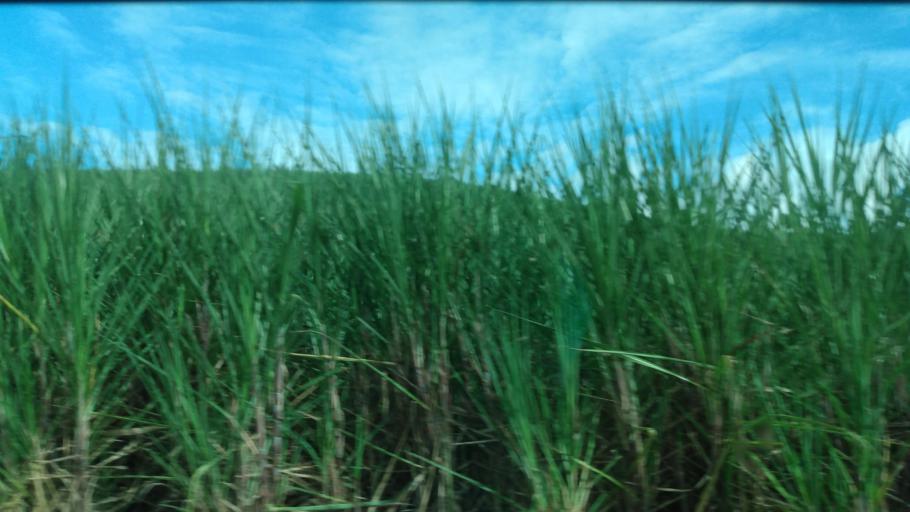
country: BR
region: Pernambuco
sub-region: Palmares
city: Palmares
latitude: -8.6945
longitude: -35.6546
